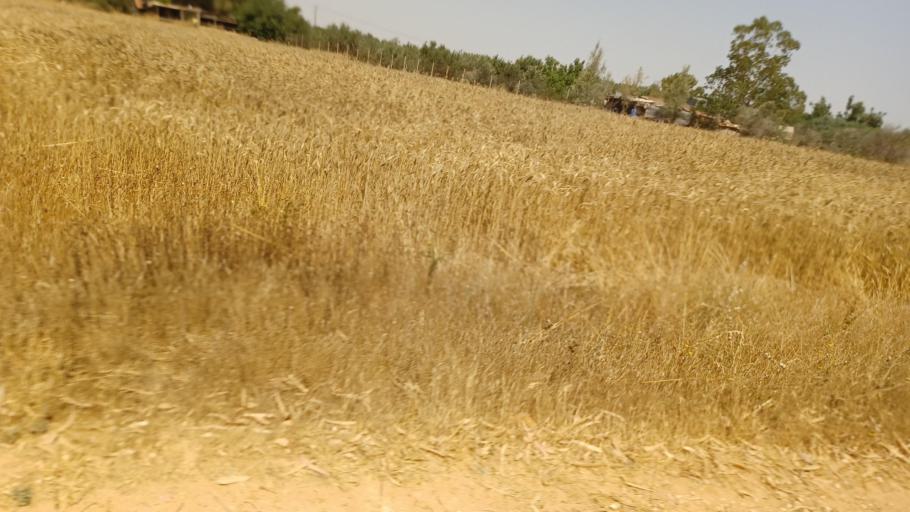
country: CY
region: Ammochostos
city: Frenaros
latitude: 35.0112
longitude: 33.9481
